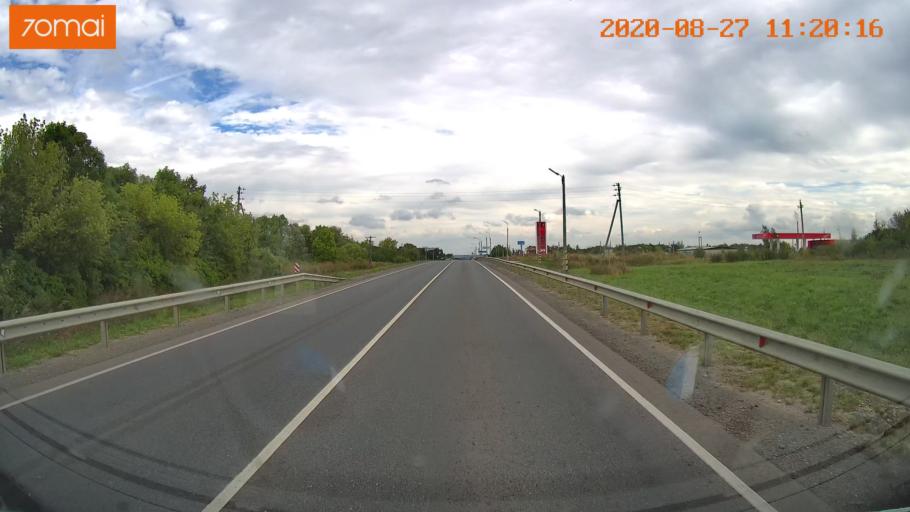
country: RU
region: Rjazan
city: Oktyabr'skiy
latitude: 54.1908
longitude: 38.9326
